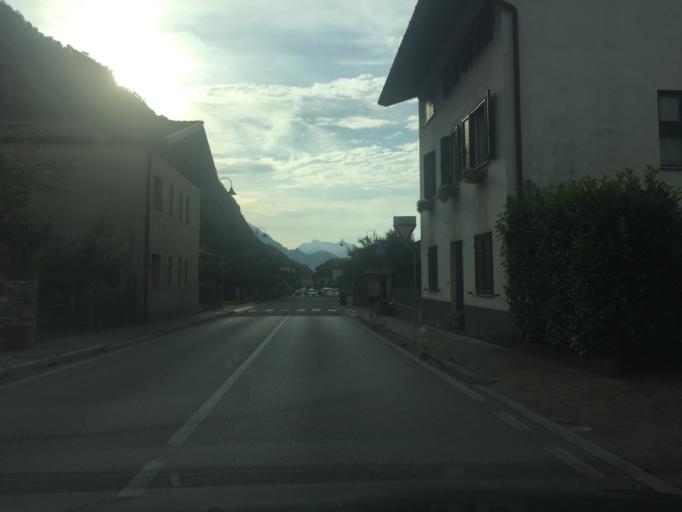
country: IT
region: Friuli Venezia Giulia
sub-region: Provincia di Udine
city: Villa Santina
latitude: 46.4172
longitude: 12.9189
